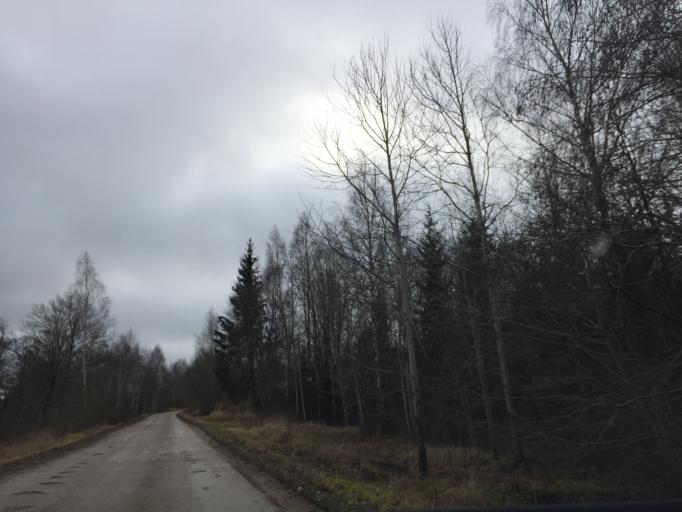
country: LV
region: Broceni
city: Broceni
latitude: 56.6610
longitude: 22.5539
